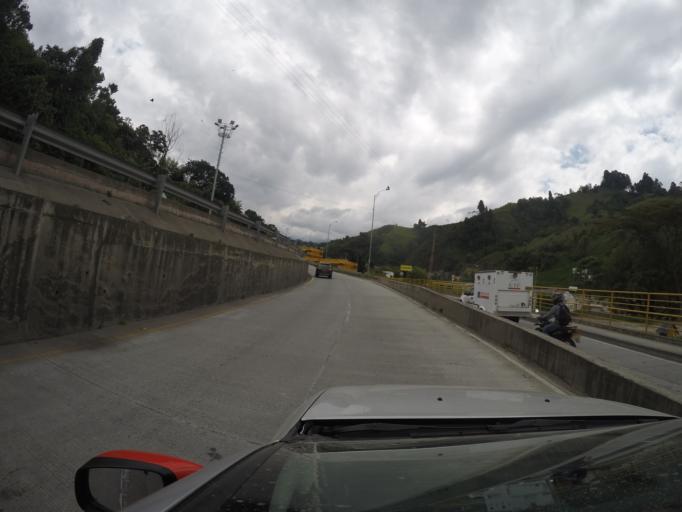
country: CO
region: Caldas
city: Villamaria
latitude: 5.0427
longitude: -75.5033
